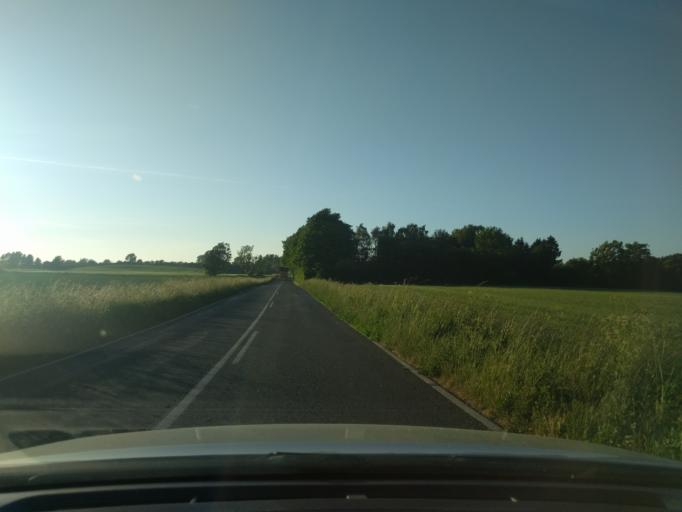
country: DK
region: South Denmark
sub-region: Kerteminde Kommune
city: Kerteminde
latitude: 55.5565
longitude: 10.6532
